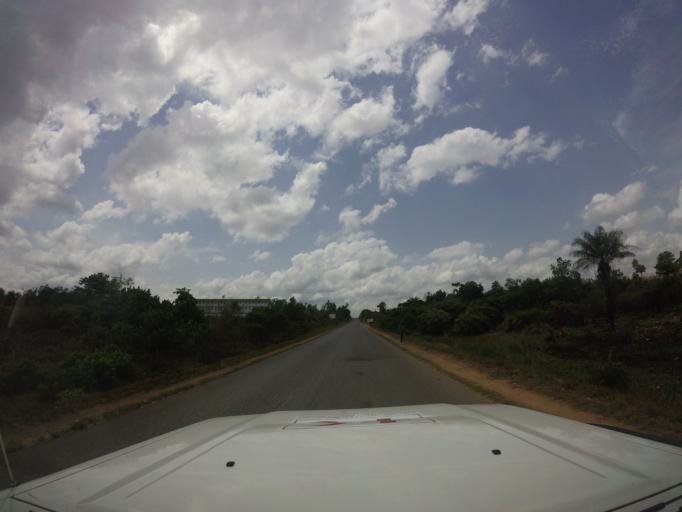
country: LR
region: Bomi
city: Tubmanburg
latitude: 6.8585
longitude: -10.8179
